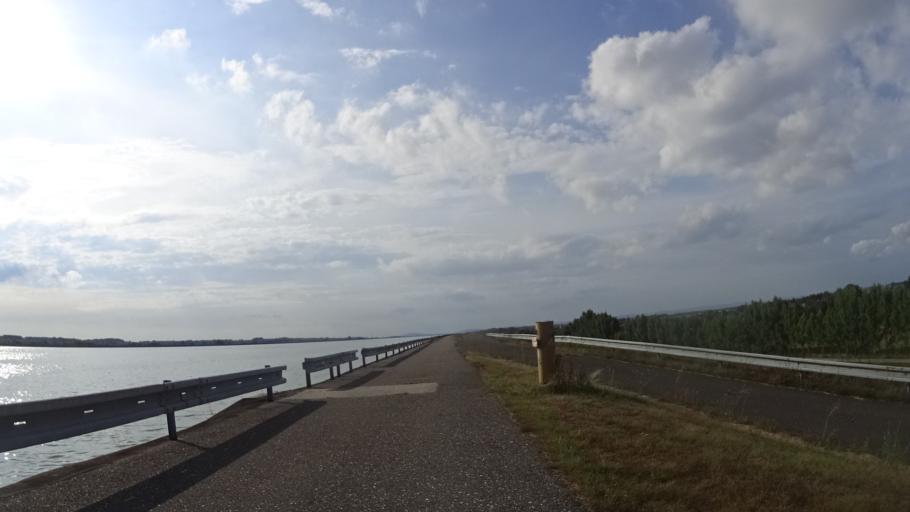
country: HU
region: Gyor-Moson-Sopron
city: Asvanyraro
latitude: 47.9448
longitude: 17.4473
